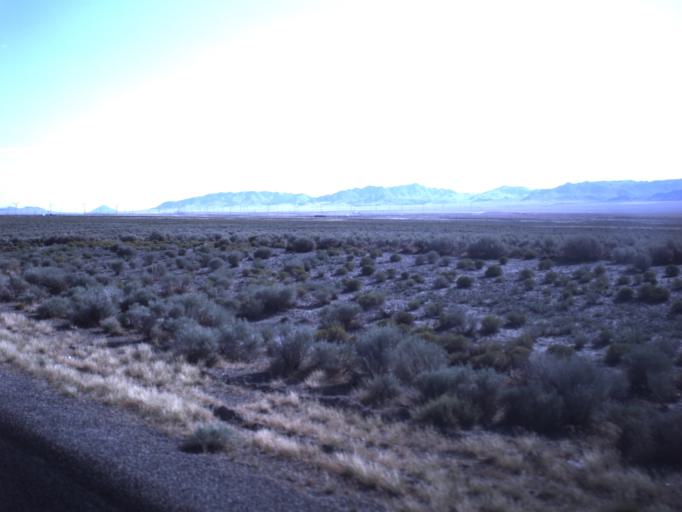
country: US
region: Utah
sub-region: Beaver County
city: Milford
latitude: 38.4439
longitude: -113.0095
